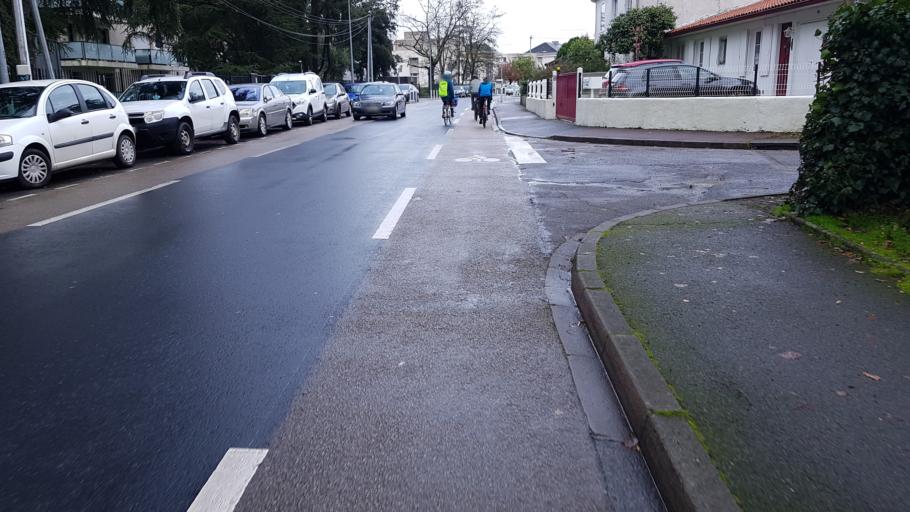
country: FR
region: Pays de la Loire
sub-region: Departement de la Loire-Atlantique
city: Saint-Sebastien-sur-Loire
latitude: 47.2043
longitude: -1.5190
